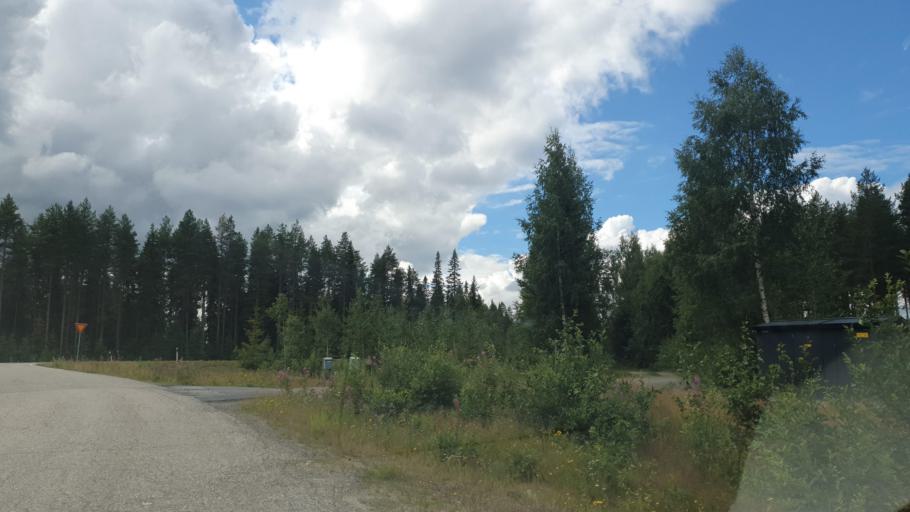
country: FI
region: Kainuu
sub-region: Kehys-Kainuu
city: Kuhmo
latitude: 64.1064
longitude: 29.3387
